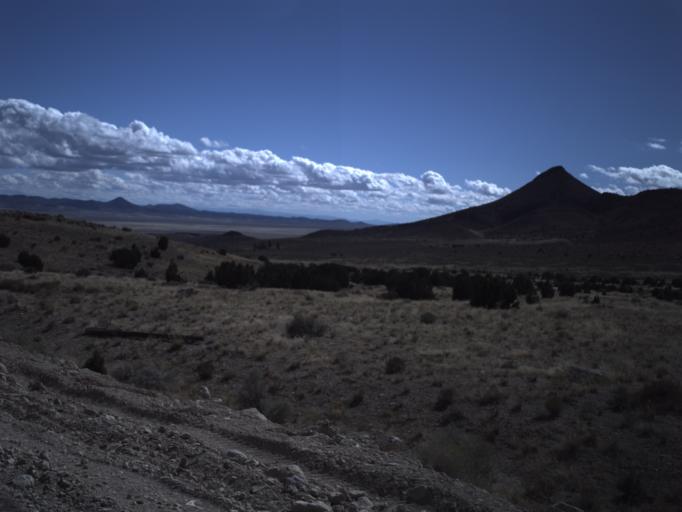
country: US
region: Utah
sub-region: Beaver County
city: Milford
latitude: 38.5040
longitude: -113.5093
